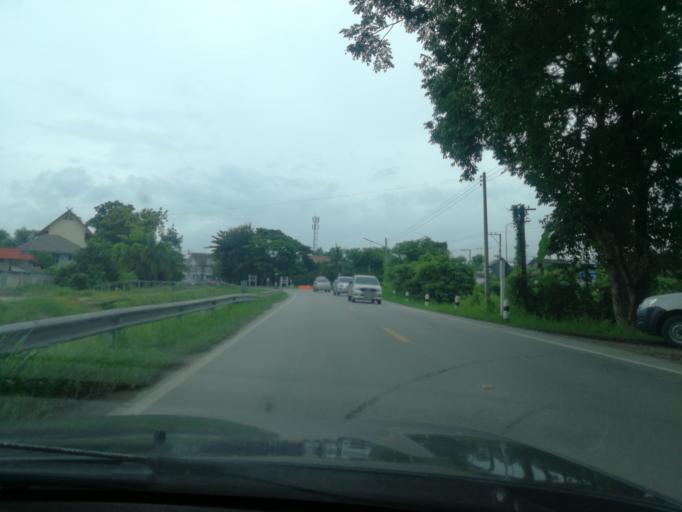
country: TH
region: Chiang Mai
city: San Pa Tong
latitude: 18.6298
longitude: 98.8987
